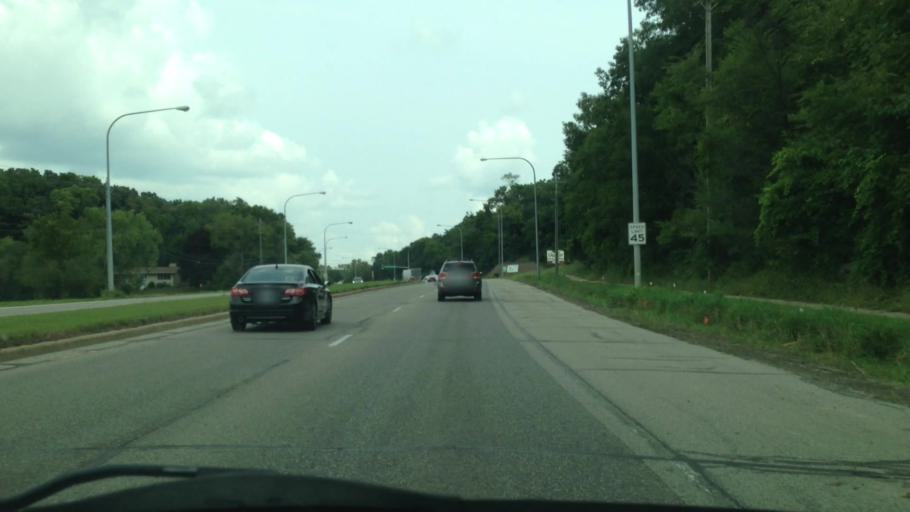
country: US
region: Minnesota
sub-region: Olmsted County
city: Rochester
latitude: 44.0454
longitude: -92.4582
